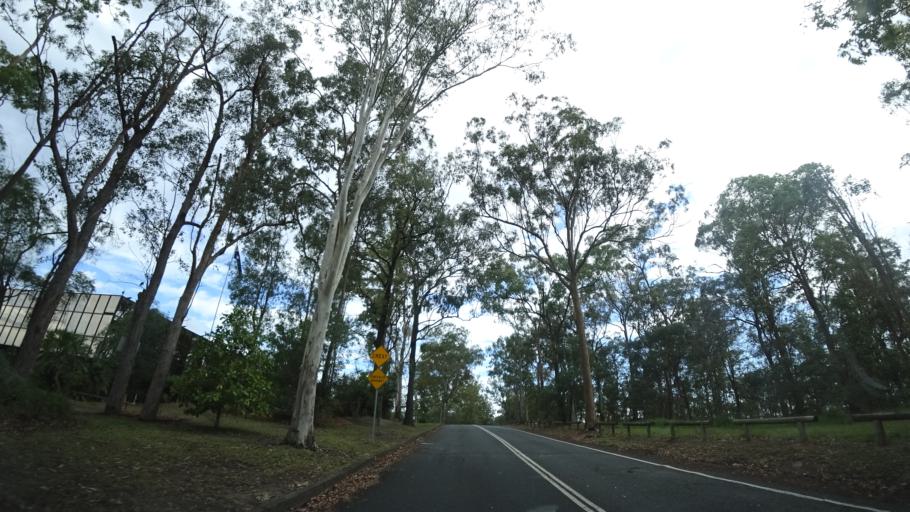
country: AU
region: Queensland
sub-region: Brisbane
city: Kenmore Hills
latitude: -27.4655
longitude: 152.9431
